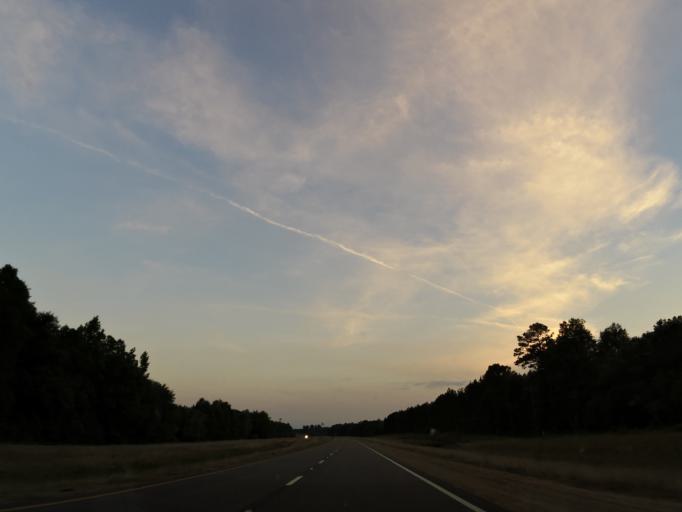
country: US
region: Mississippi
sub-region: Kemper County
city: De Kalb
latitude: 32.7666
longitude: -88.4642
